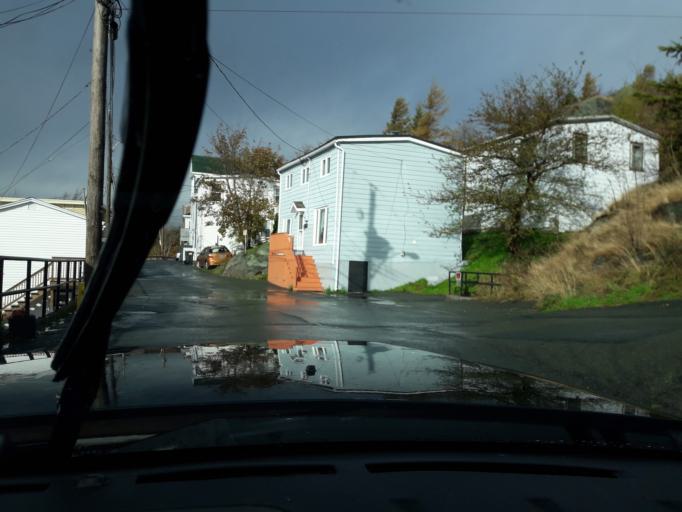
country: CA
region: Newfoundland and Labrador
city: St. John's
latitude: 47.5701
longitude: -52.6921
